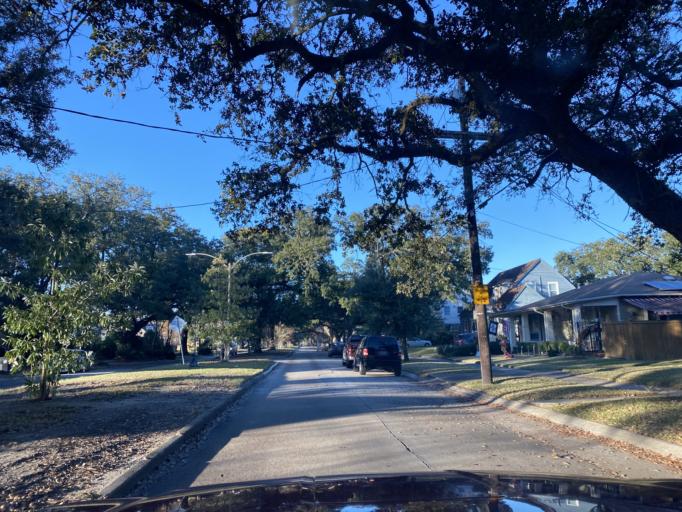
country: US
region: Louisiana
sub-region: Orleans Parish
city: New Orleans
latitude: 30.0090
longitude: -90.0554
